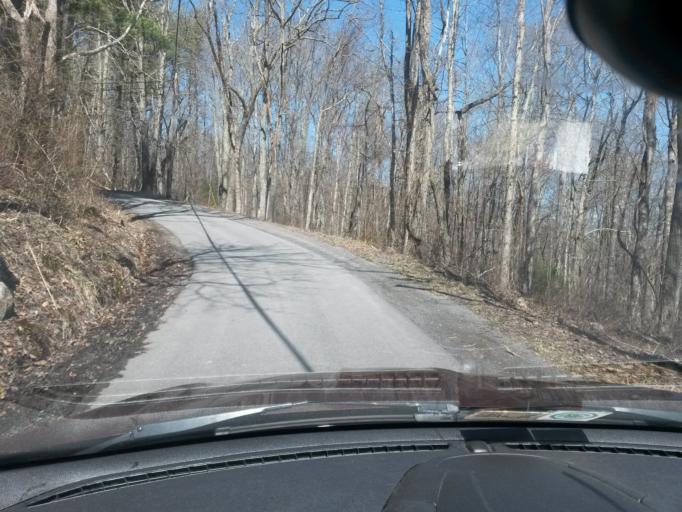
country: US
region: West Virginia
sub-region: Greenbrier County
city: White Sulphur Springs
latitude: 37.6754
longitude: -80.3220
